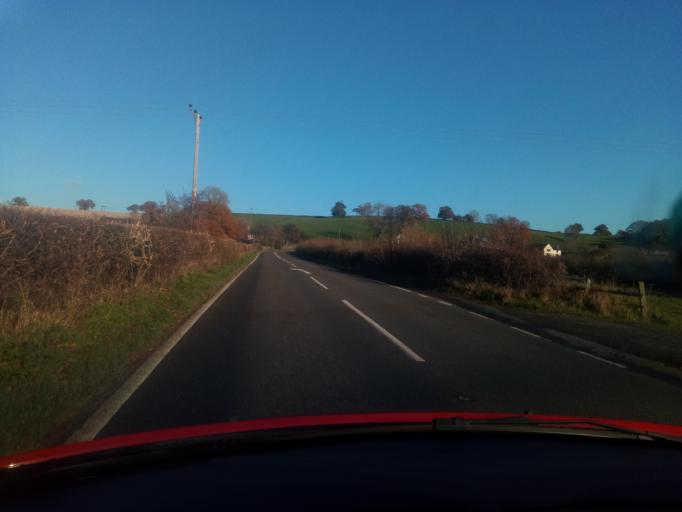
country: GB
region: England
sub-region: Derbyshire
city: Belper
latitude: 53.0219
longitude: -1.5369
